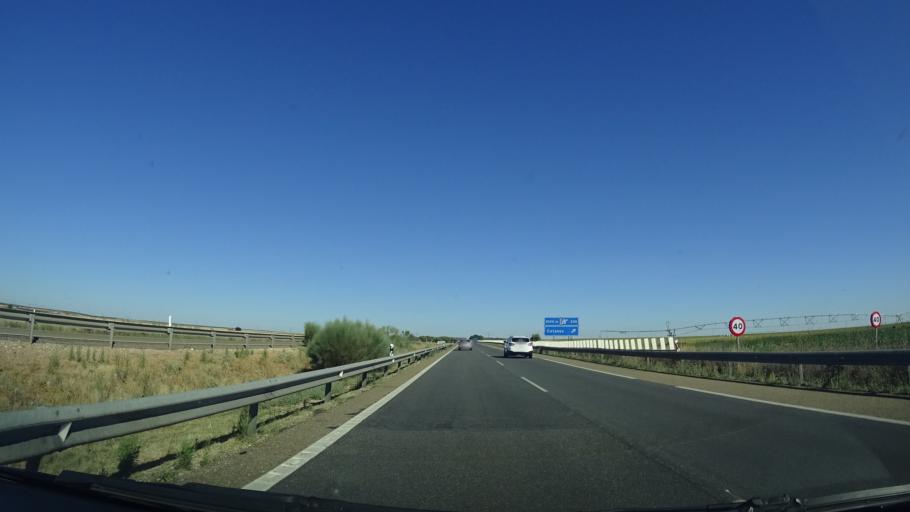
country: ES
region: Castille and Leon
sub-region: Provincia de Valladolid
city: San Pedro de Latarce
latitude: 41.7905
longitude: -5.3315
